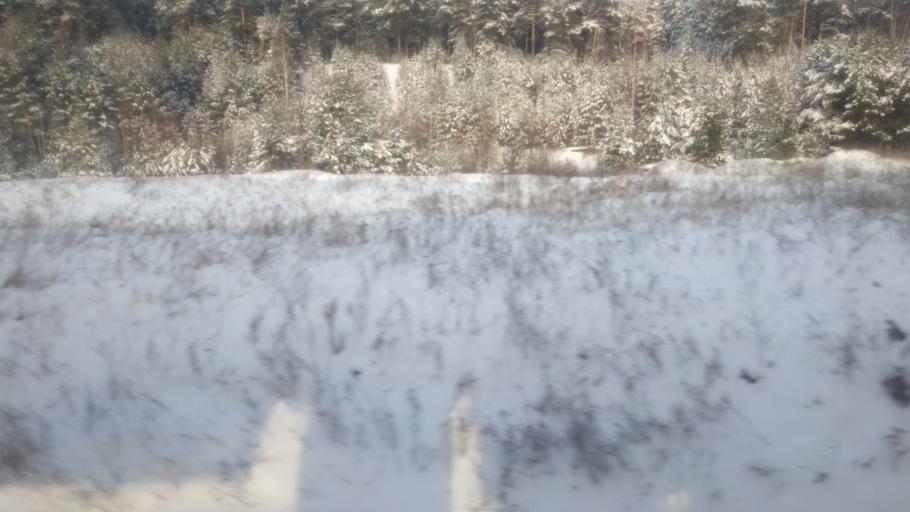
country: RU
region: Kirov
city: Krasnaya Polyana
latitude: 56.2476
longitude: 51.1610
